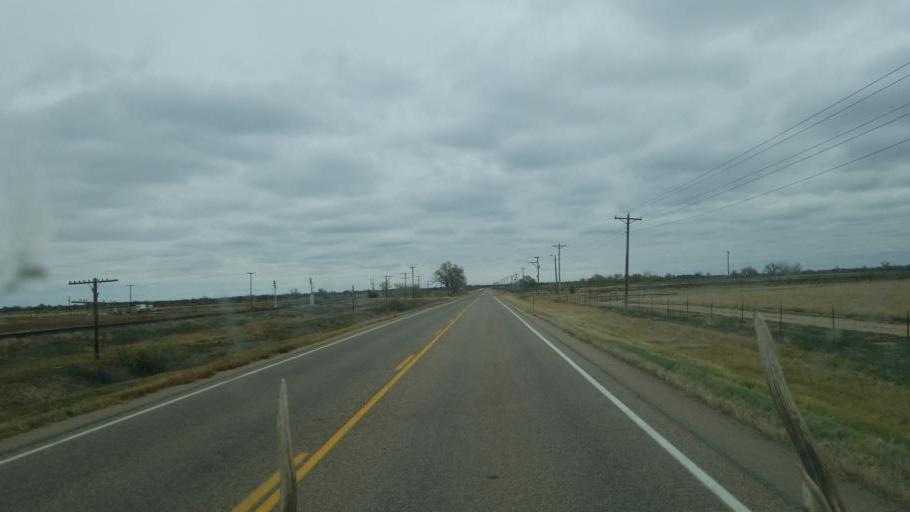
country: US
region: Colorado
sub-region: Crowley County
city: Ordway
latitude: 38.1965
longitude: -103.8411
